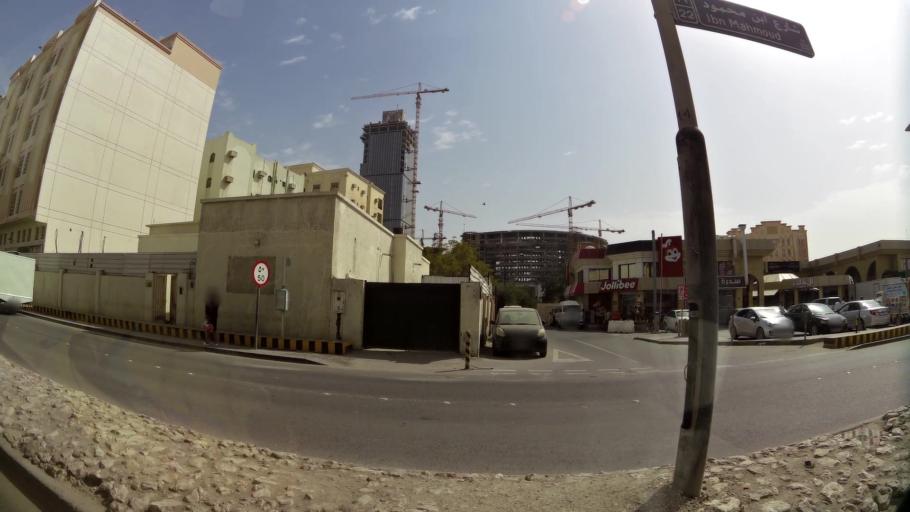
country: QA
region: Baladiyat ad Dawhah
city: Doha
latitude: 25.2843
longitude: 51.5145
